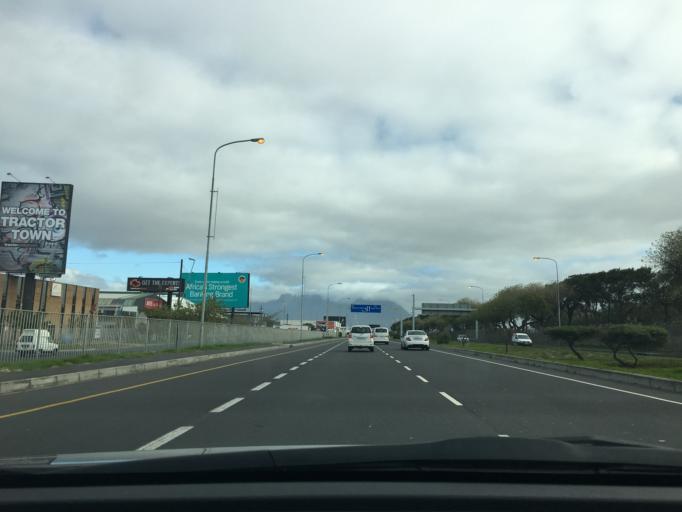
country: ZA
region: Western Cape
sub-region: City of Cape Town
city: Lansdowne
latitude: -33.9683
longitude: 18.5837
